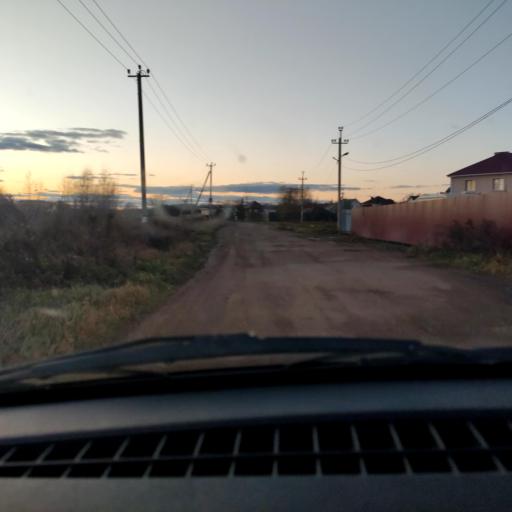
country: RU
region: Bashkortostan
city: Ufa
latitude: 54.6443
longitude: 55.9152
